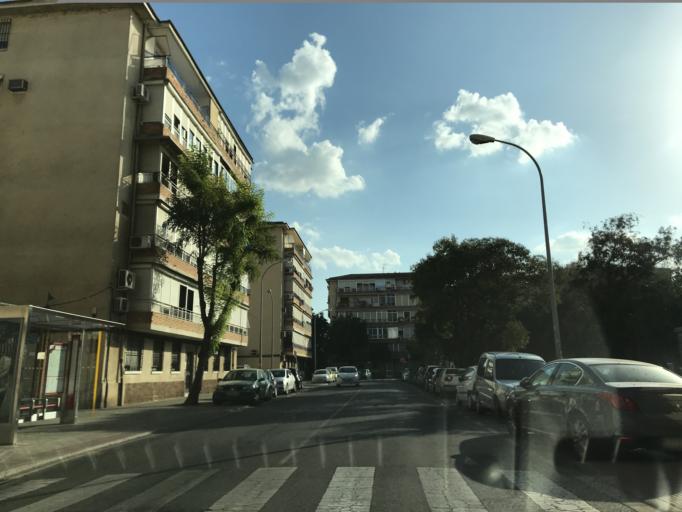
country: ES
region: Andalusia
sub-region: Provincia de Sevilla
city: Sevilla
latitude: 37.4123
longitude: -5.9293
